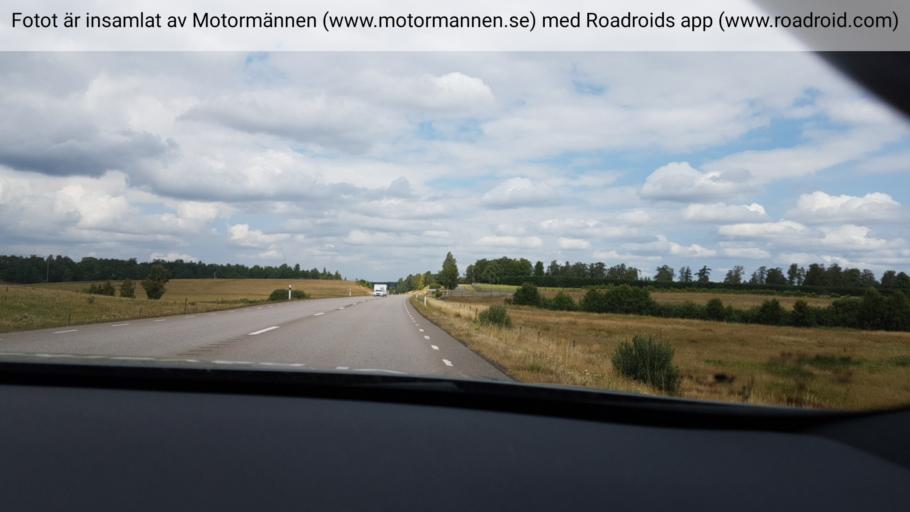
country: SE
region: Vaestra Goetaland
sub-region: Skara Kommun
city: Skara
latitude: 58.2793
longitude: 13.4851
